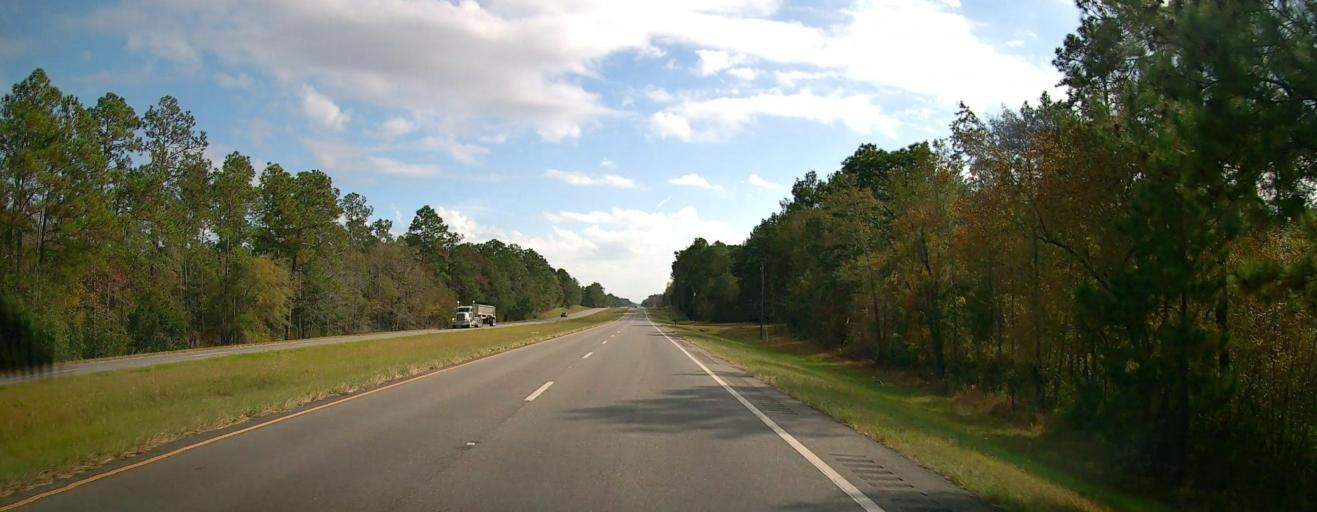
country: US
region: Georgia
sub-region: Thomas County
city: Meigs
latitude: 30.9997
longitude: -84.0478
